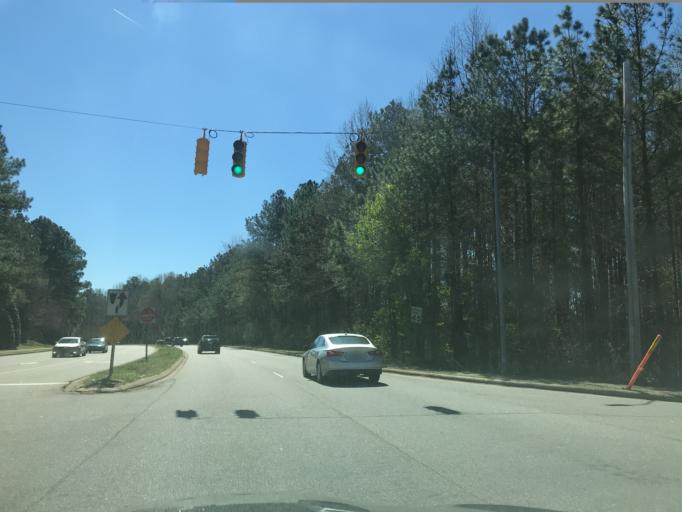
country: US
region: North Carolina
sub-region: Wake County
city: Garner
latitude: 35.6894
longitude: -78.6339
